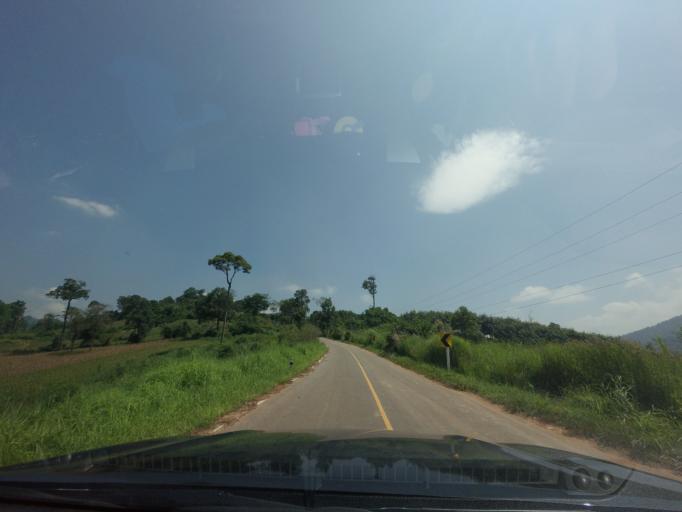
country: TH
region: Loei
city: Na Haeo
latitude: 17.5688
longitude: 100.8937
